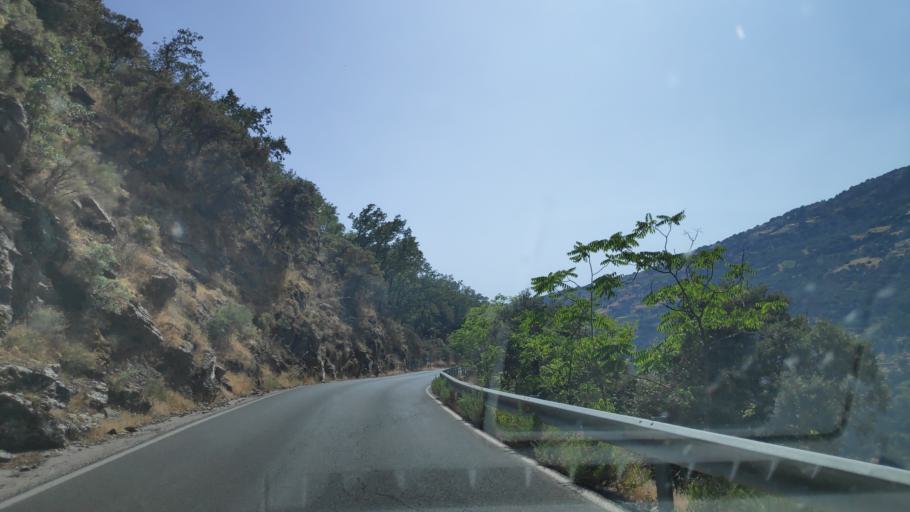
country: ES
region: Andalusia
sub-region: Provincia de Granada
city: Pampaneira
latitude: 36.9377
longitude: -3.3581
